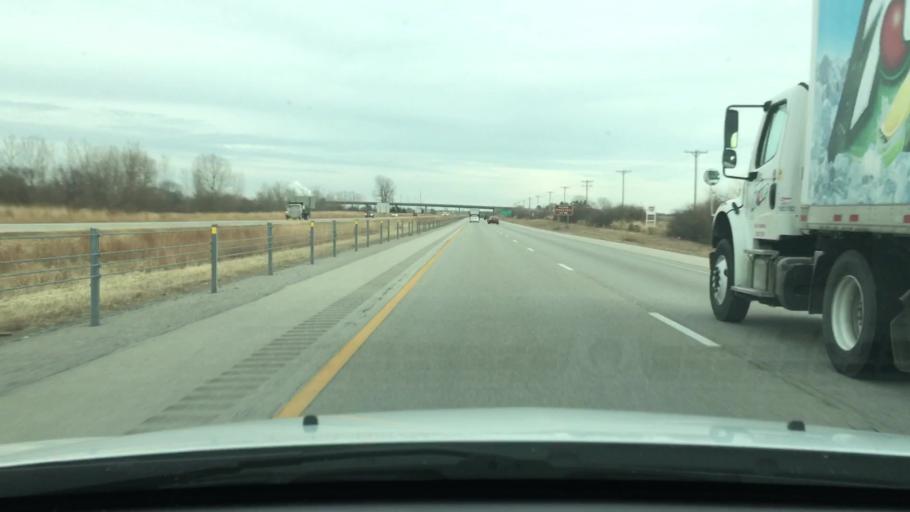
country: US
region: Illinois
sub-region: Sangamon County
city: Jerome
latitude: 39.7418
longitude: -89.6958
